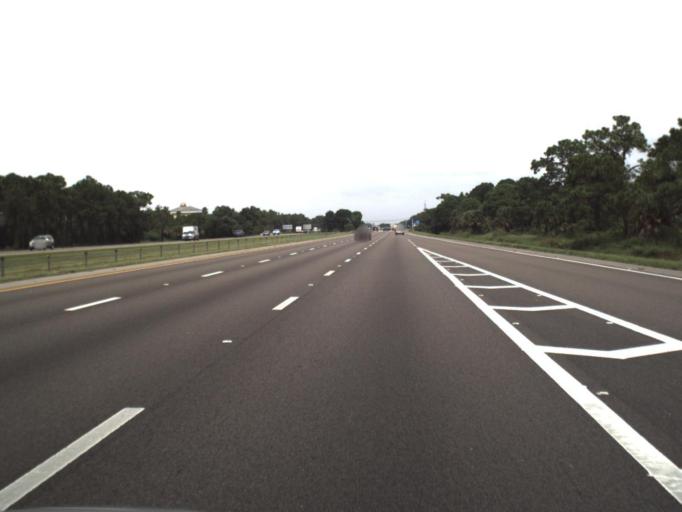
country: US
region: Florida
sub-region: Sarasota County
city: The Meadows
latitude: 27.3934
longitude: -82.4499
